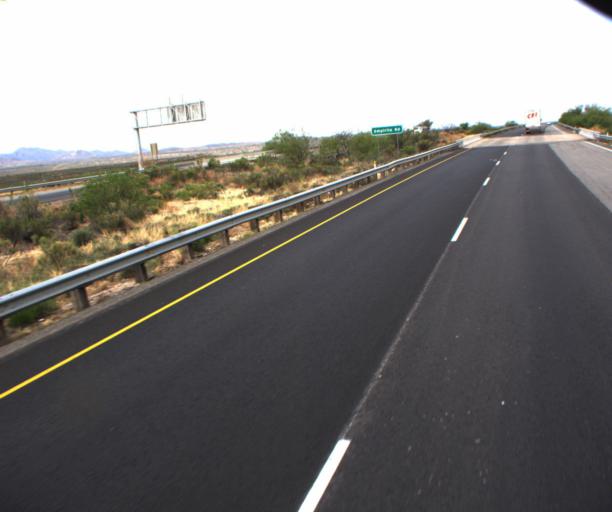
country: US
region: Arizona
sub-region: Cochise County
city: Mescal
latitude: 31.9767
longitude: -110.5112
